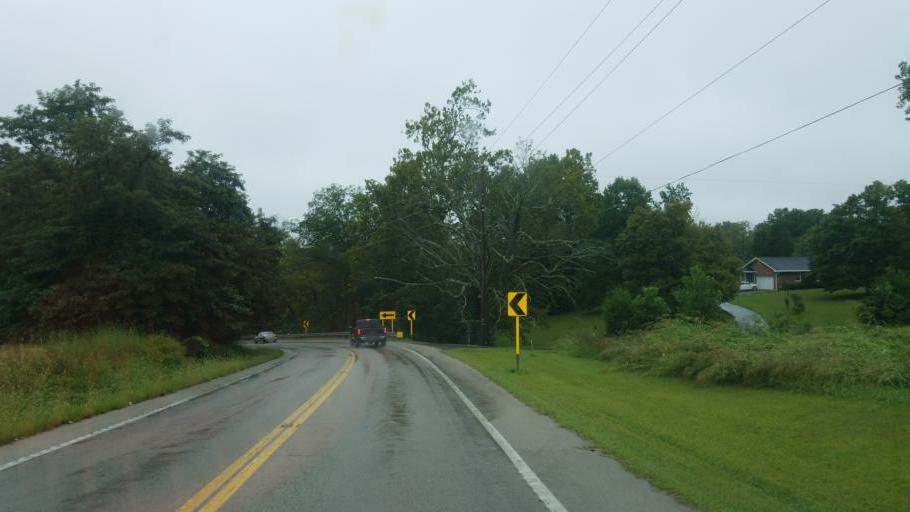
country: US
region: Ohio
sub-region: Adams County
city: West Union
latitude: 38.7986
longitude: -83.5044
